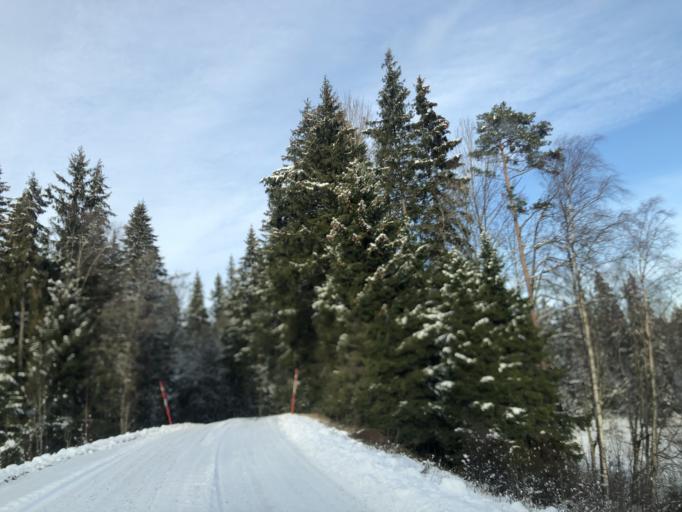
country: SE
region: Vaestra Goetaland
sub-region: Ulricehamns Kommun
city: Ulricehamn
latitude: 57.7741
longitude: 13.5235
